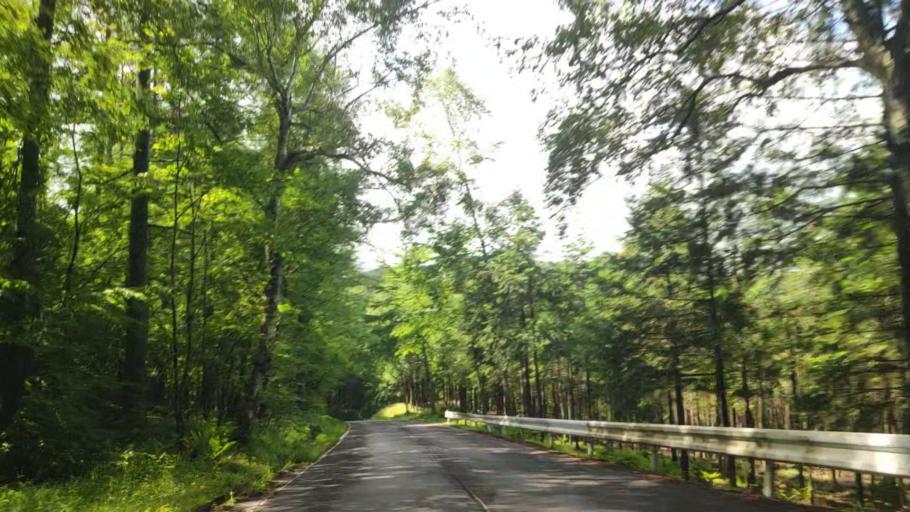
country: JP
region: Nagano
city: Suwa
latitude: 36.0887
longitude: 138.1474
